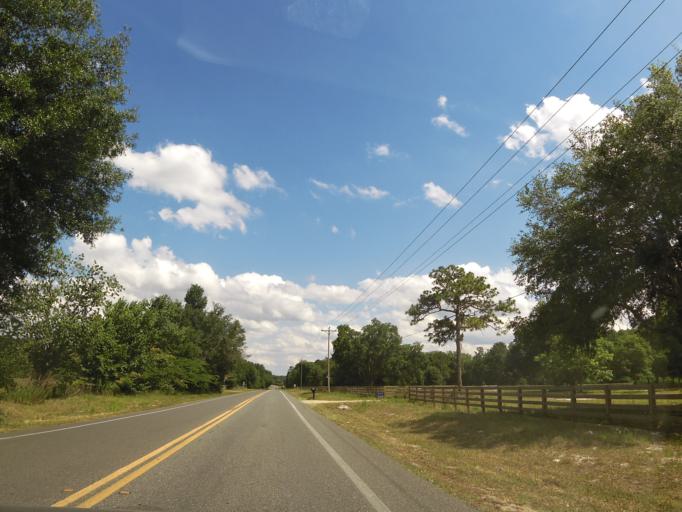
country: US
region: Florida
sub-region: Clay County
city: Keystone Heights
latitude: 29.8766
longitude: -81.9261
